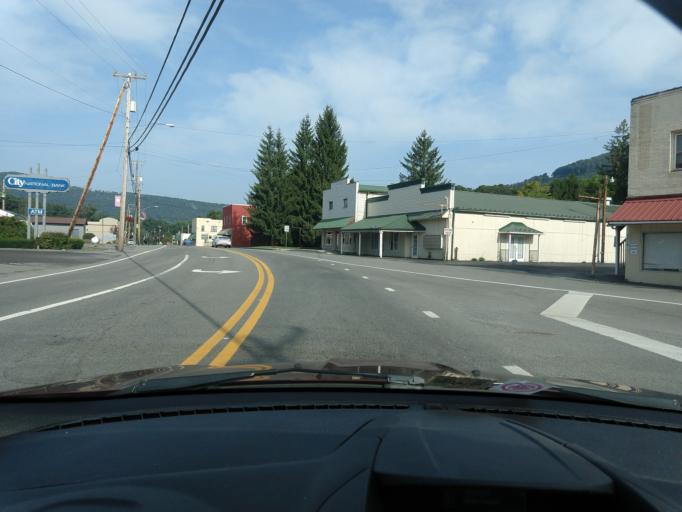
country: US
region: West Virginia
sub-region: Greenbrier County
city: Rainelle
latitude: 37.9642
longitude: -80.6908
